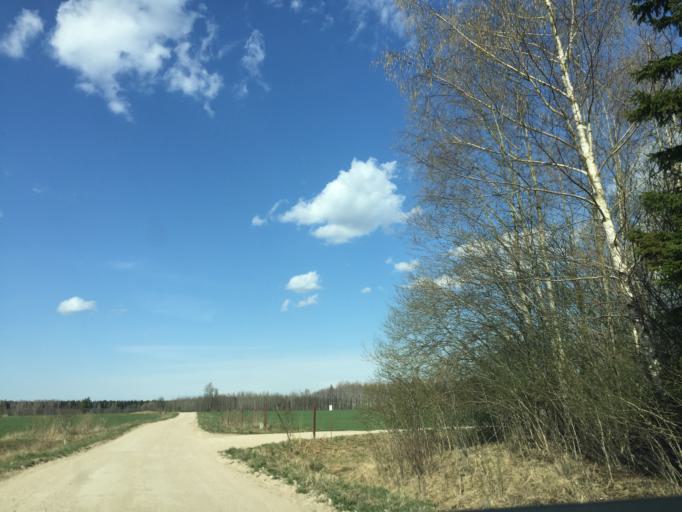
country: LV
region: Lielvarde
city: Lielvarde
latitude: 56.8292
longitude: 24.7960
